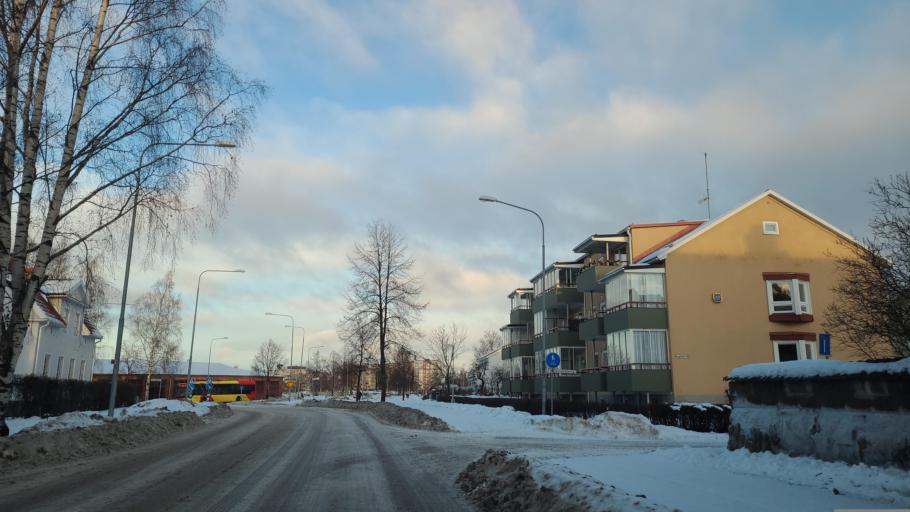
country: SE
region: Gaevleborg
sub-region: Bollnas Kommun
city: Bollnas
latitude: 61.3517
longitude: 16.3998
